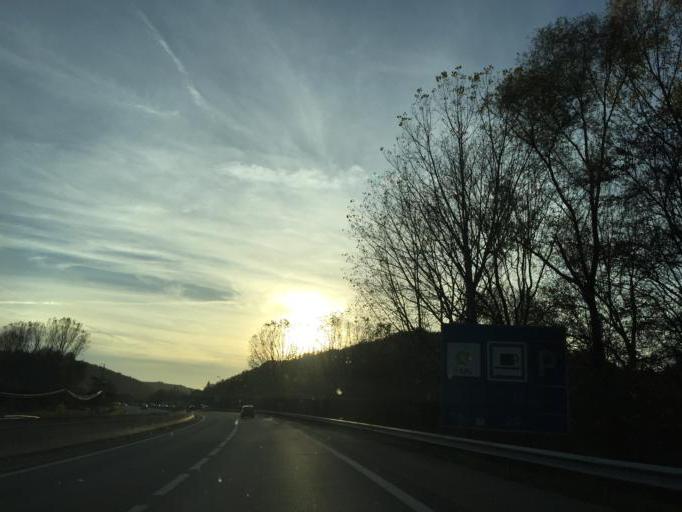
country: FR
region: Rhone-Alpes
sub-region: Departement du Rhone
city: Echalas
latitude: 45.5742
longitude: 4.7159
